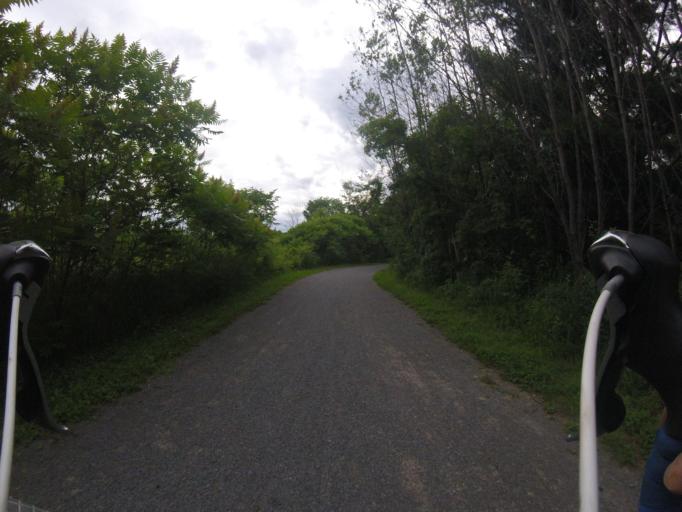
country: CA
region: Ontario
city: Bells Corners
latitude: 45.3285
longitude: -75.7996
